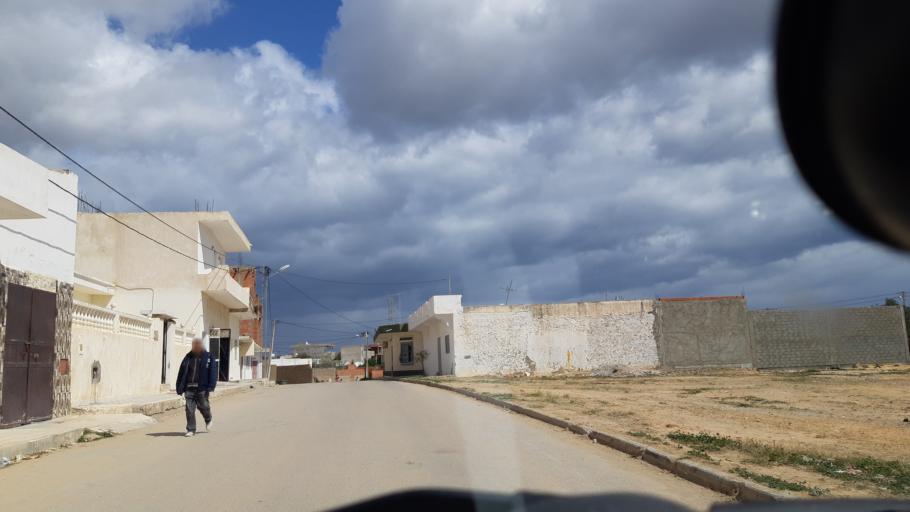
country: TN
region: Susah
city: Akouda
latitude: 35.8820
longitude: 10.5382
